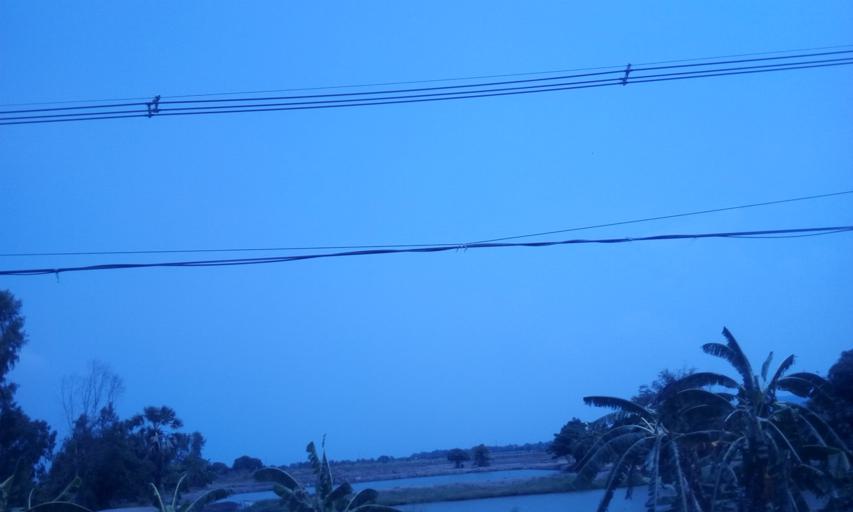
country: TH
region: Chon Buri
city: Phan Thong
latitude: 13.5352
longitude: 101.1490
